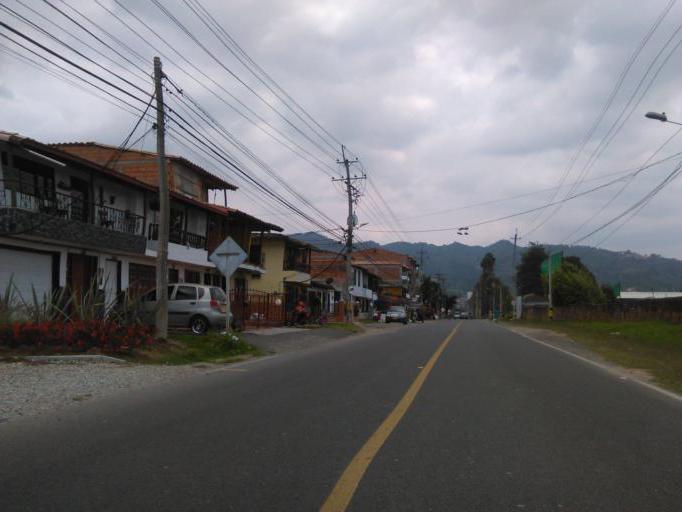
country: CO
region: Antioquia
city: La Ceja
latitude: 6.0277
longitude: -75.4230
